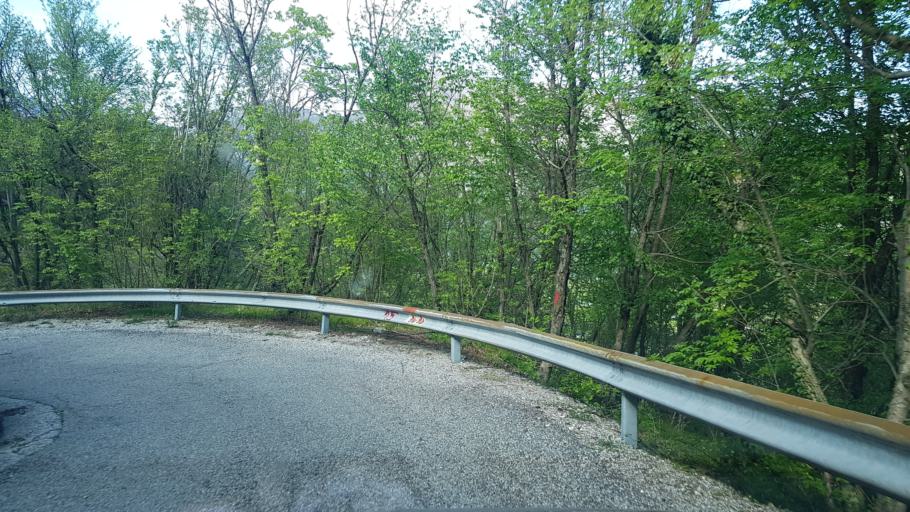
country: IT
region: Friuli Venezia Giulia
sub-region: Provincia di Udine
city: Trasaghis
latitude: 46.3139
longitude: 13.0439
